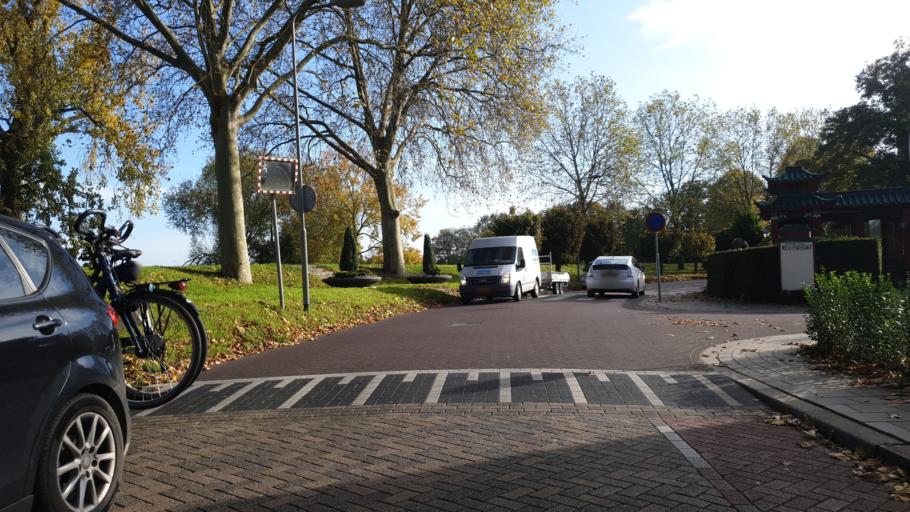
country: NL
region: Limburg
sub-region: Gemeente Gennep
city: Gennep
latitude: 51.7014
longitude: 5.9717
